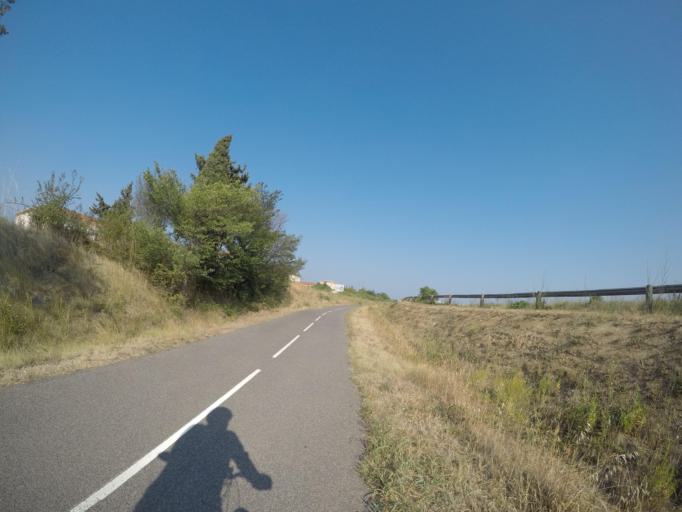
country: FR
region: Languedoc-Roussillon
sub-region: Departement des Pyrenees-Orientales
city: Llupia
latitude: 42.6224
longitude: 2.7738
